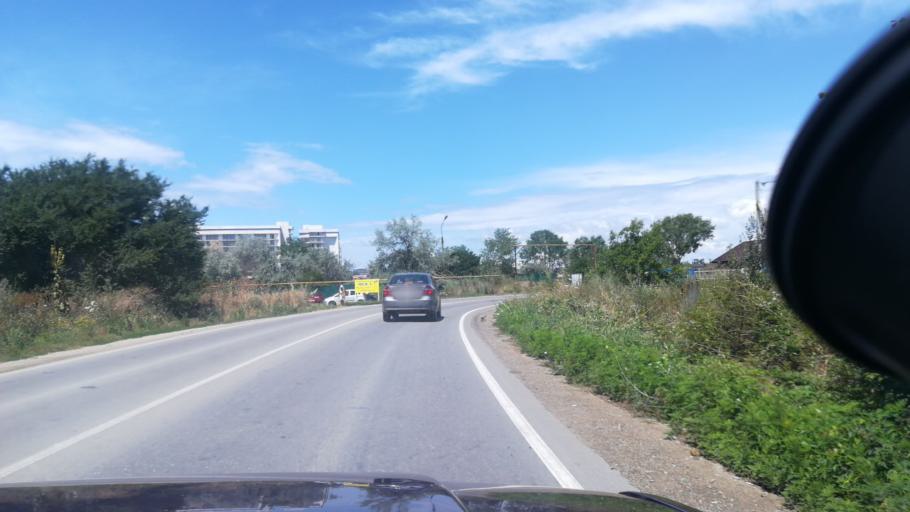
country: RU
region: Krasnodarskiy
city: Vityazevo
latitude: 44.9636
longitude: 37.2914
